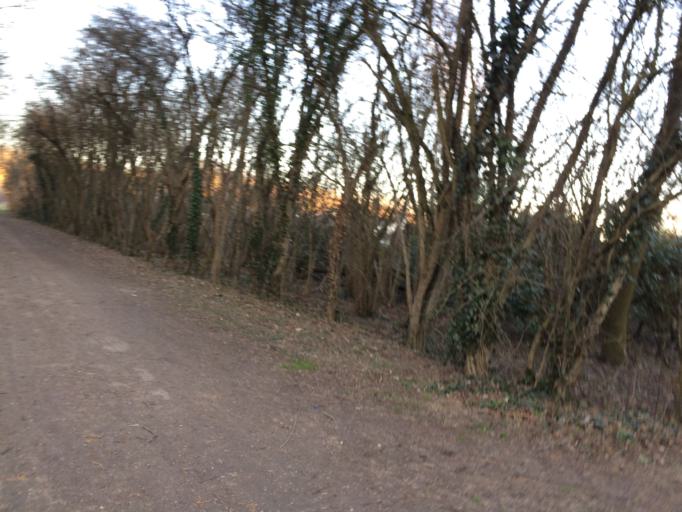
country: FR
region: Ile-de-France
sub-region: Departement de l'Essonne
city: Villebon-sur-Yvette
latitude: 48.7113
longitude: 2.2261
